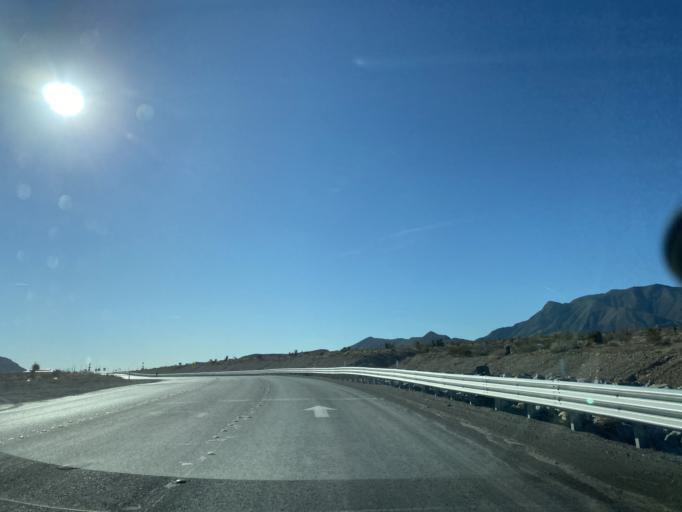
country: US
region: Nevada
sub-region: Clark County
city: Summerlin South
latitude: 36.2631
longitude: -115.3303
